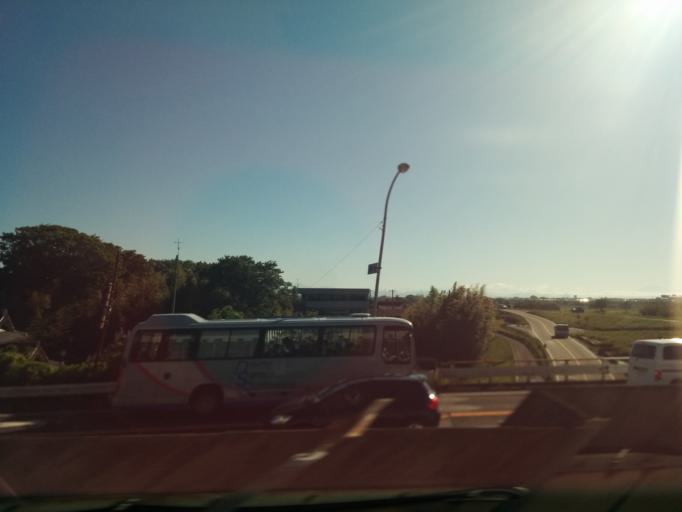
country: JP
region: Gifu
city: Ogaki
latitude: 35.3259
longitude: 136.6740
